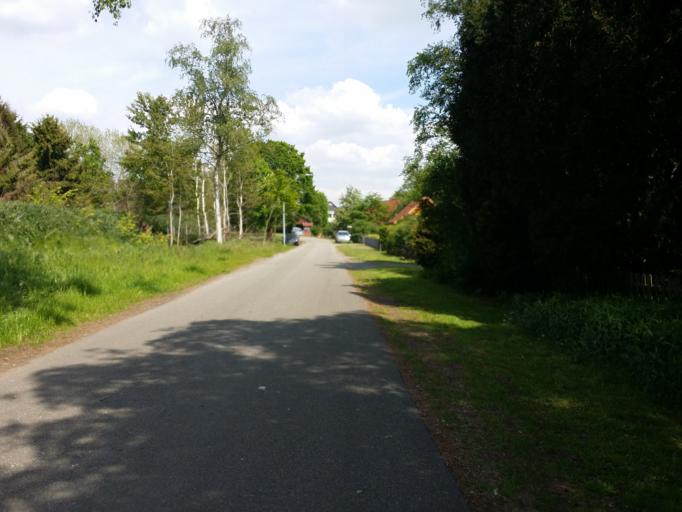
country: DE
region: Lower Saxony
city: Hambergen
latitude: 53.2909
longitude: 8.8370
